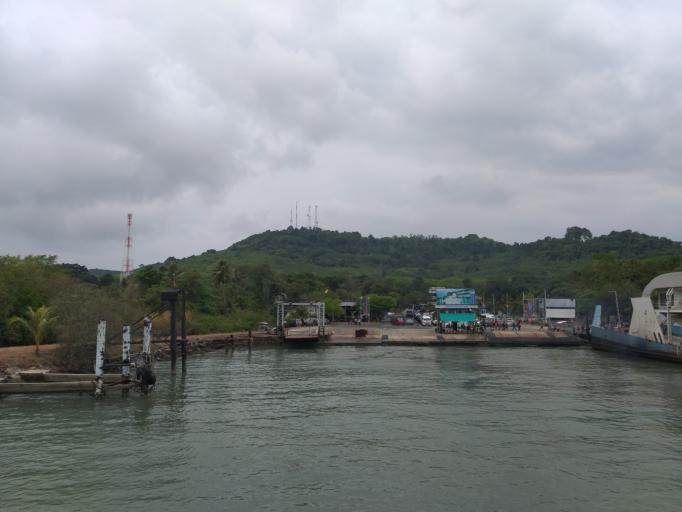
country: TH
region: Trat
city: Laem Ngop
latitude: 12.1863
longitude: 102.3013
